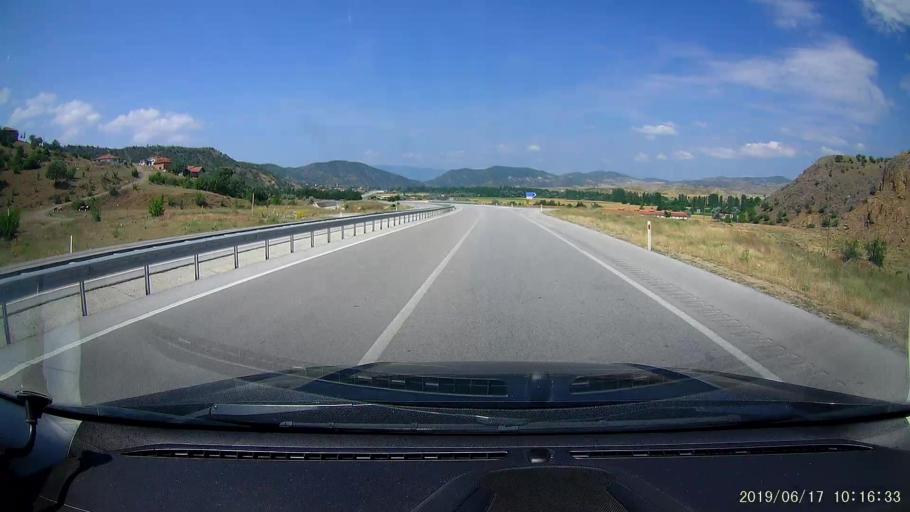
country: TR
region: Corum
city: Osmancik
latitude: 40.9896
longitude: 34.9724
